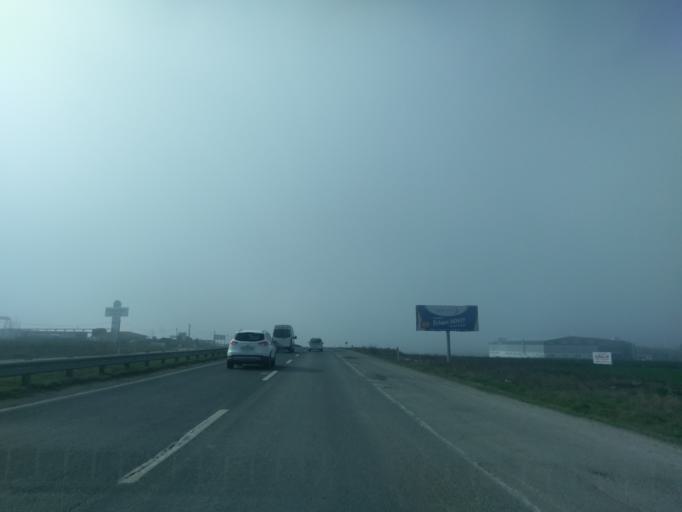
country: TR
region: Istanbul
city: Kavakli
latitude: 41.0653
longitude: 28.3179
